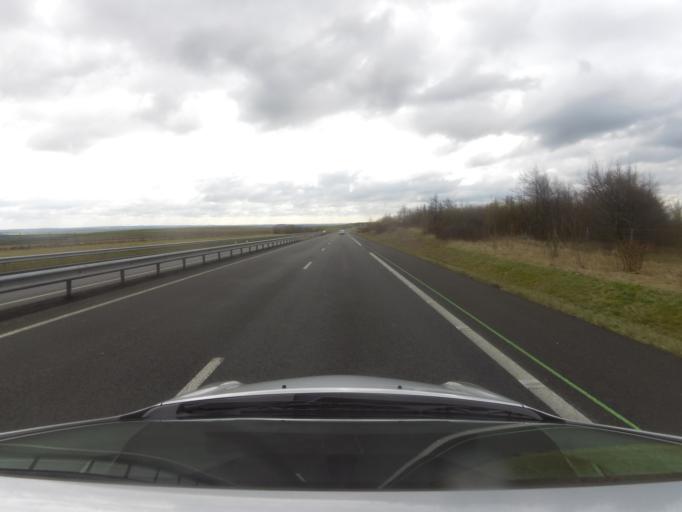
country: FR
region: Nord-Pas-de-Calais
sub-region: Departement du Pas-de-Calais
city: Camiers
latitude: 50.5696
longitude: 1.6519
